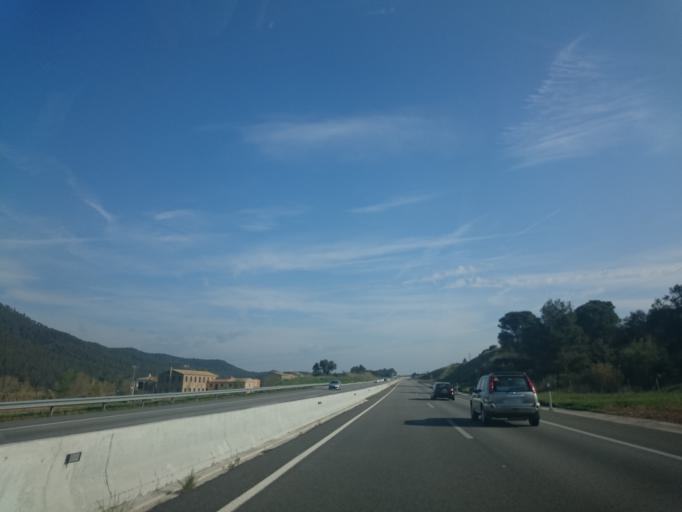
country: ES
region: Catalonia
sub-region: Provincia de Barcelona
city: Artes
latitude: 41.8186
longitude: 1.9662
